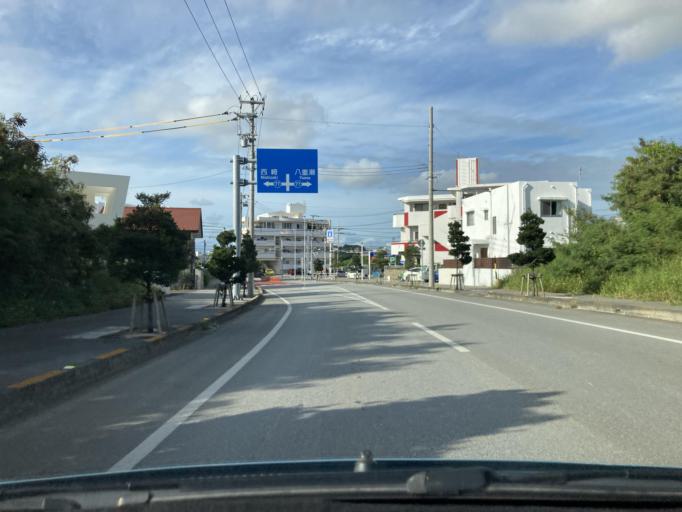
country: JP
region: Okinawa
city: Itoman
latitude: 26.1305
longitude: 127.6837
